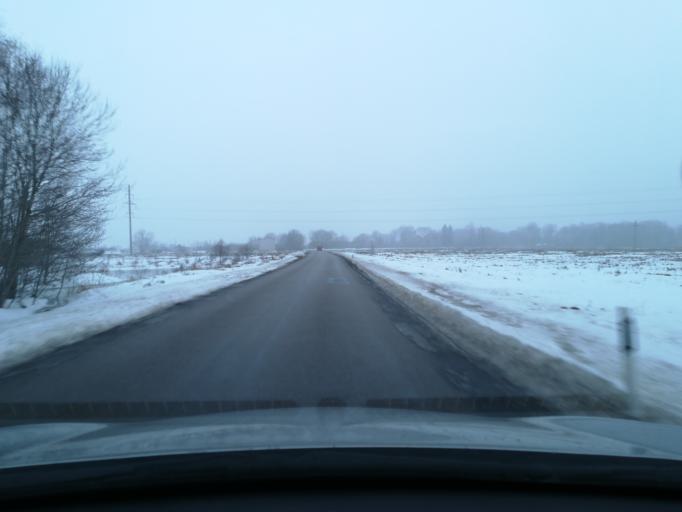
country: EE
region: Harju
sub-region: Rae vald
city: Jueri
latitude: 59.3770
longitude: 24.8947
